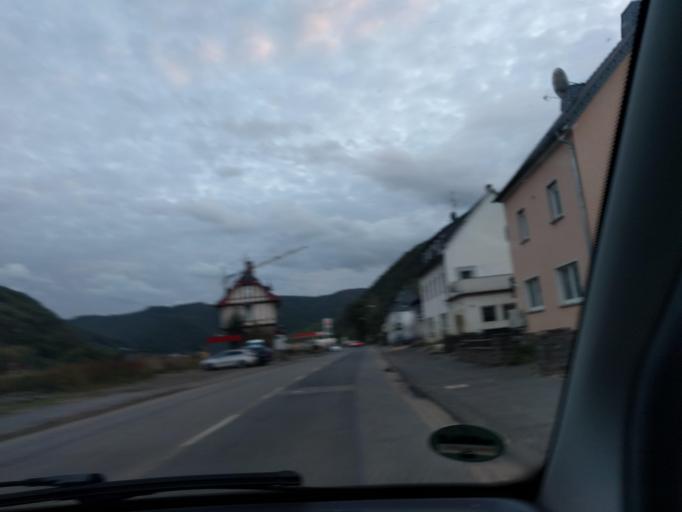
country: DE
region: Rheinland-Pfalz
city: Dernau
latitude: 50.5307
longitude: 7.0420
